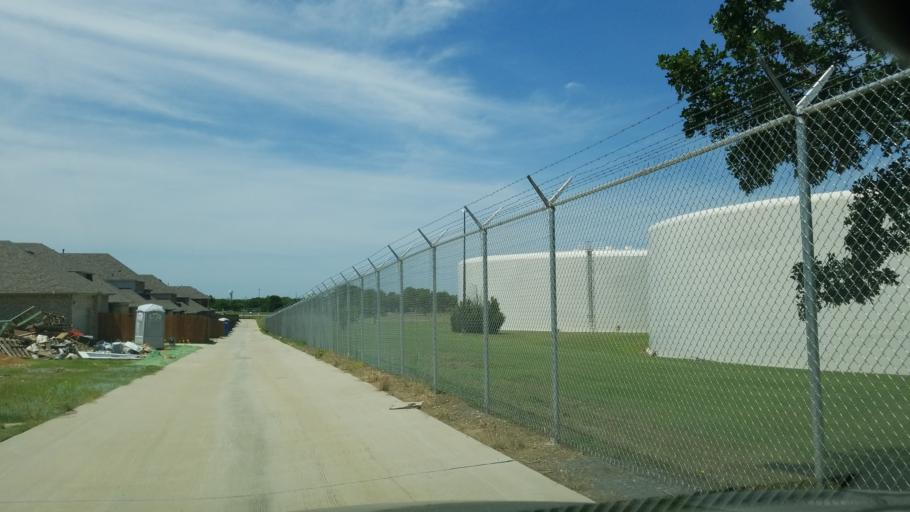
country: US
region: Texas
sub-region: Dallas County
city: Coppell
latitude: 32.8782
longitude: -96.9949
